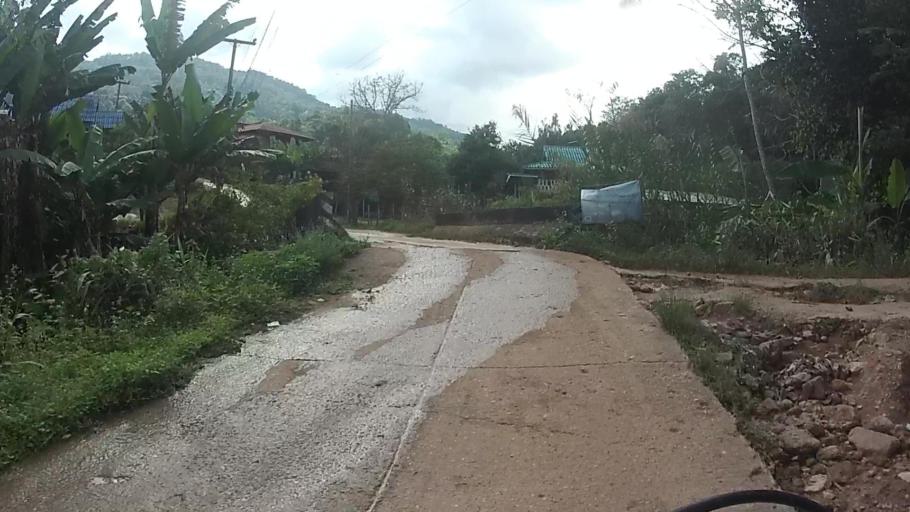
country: TH
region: Lampang
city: Mueang Pan
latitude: 18.9095
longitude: 99.4087
